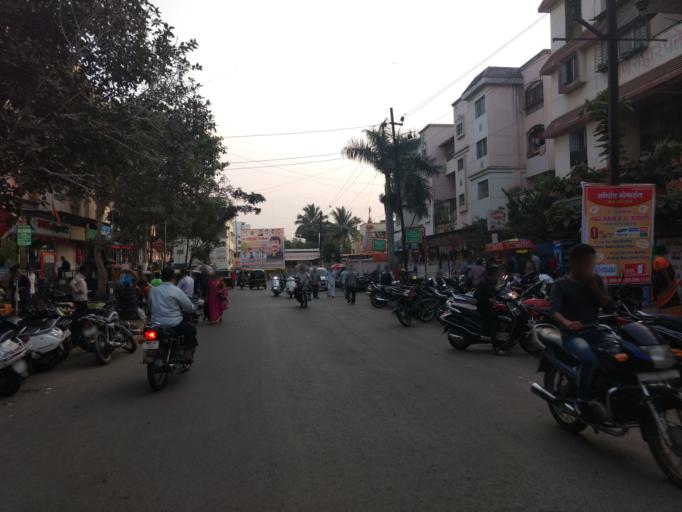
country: IN
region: Maharashtra
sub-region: Pune Division
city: Pune
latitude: 18.4564
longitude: 73.8695
